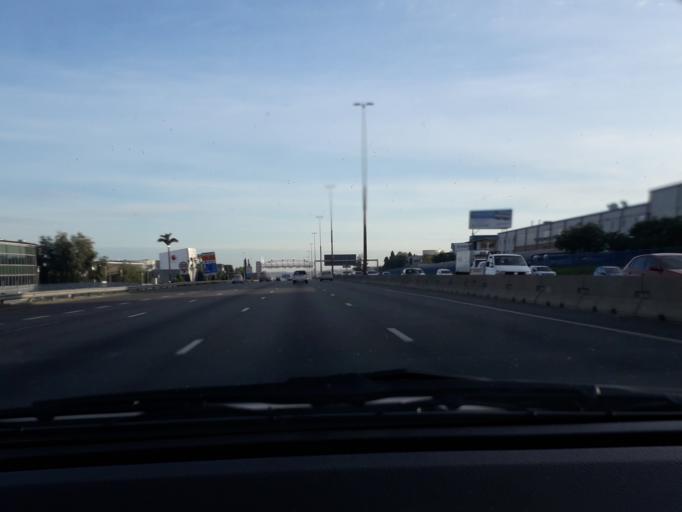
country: ZA
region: Gauteng
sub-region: City of Johannesburg Metropolitan Municipality
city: Midrand
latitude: -25.9731
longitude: 28.1284
